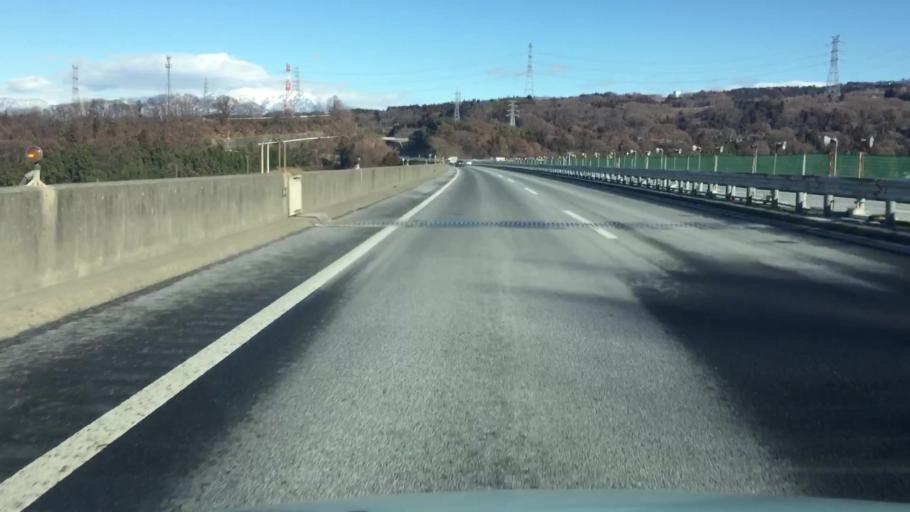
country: JP
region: Gunma
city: Numata
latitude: 36.5582
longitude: 139.0588
